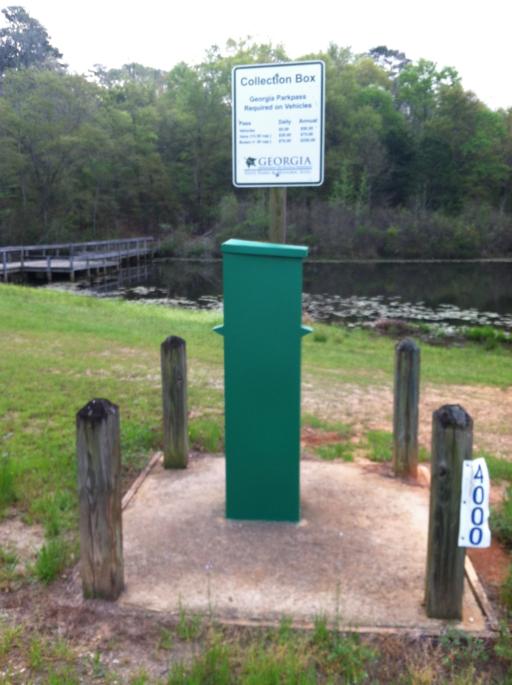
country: US
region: Georgia
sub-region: Early County
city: Blakely
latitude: 31.4645
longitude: -84.9200
